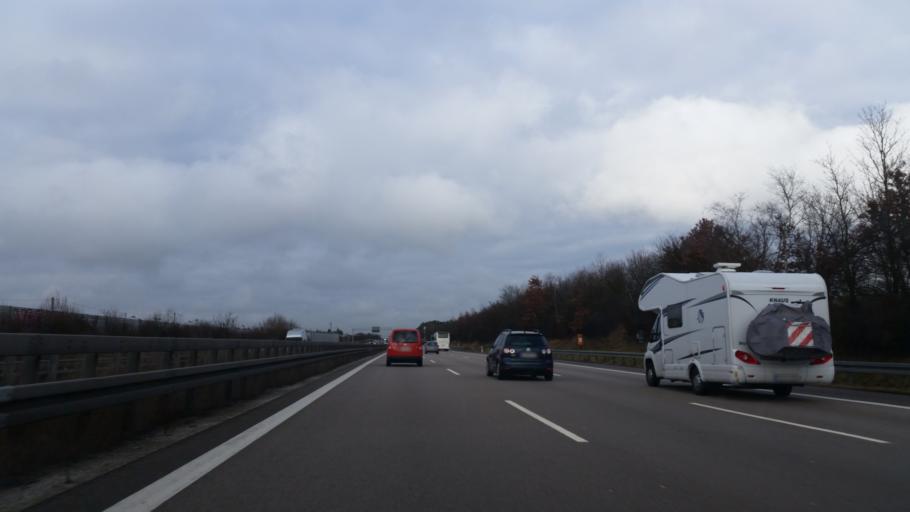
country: DE
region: Bavaria
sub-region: Regierungsbezirk Mittelfranken
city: Allersberg
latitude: 49.2597
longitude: 11.2140
